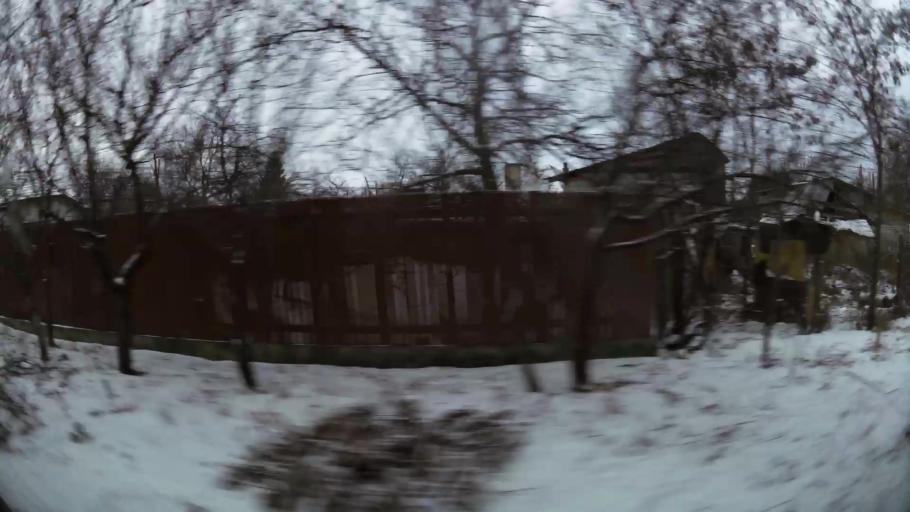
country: RO
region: Prahova
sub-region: Comuna Berceni
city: Corlatesti
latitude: 44.9256
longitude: 26.0657
